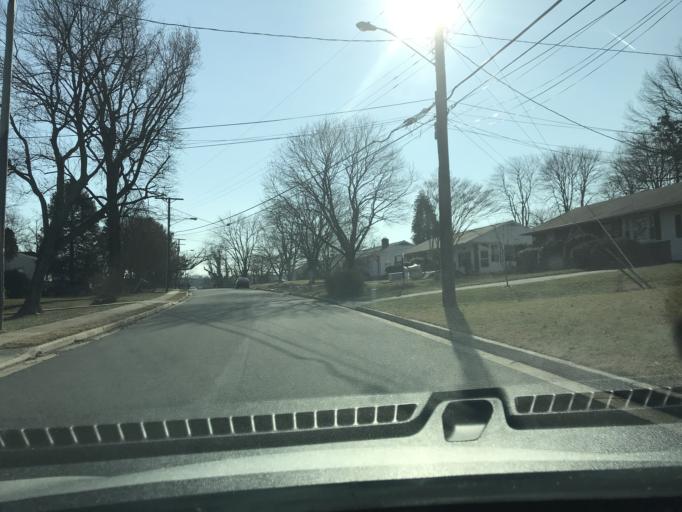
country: US
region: Virginia
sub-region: City of Fairfax
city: Fairfax
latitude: 38.8559
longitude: -77.3226
